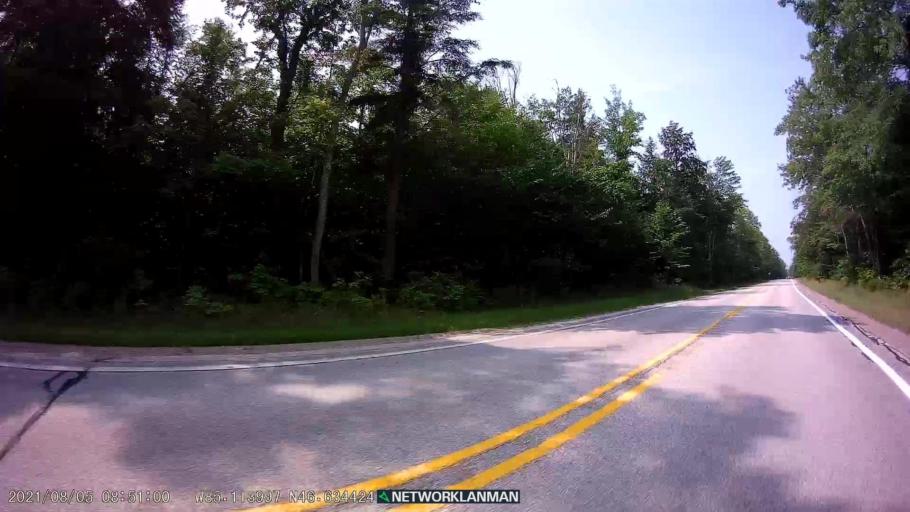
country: US
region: Michigan
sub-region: Luce County
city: Newberry
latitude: 46.6342
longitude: -85.1154
